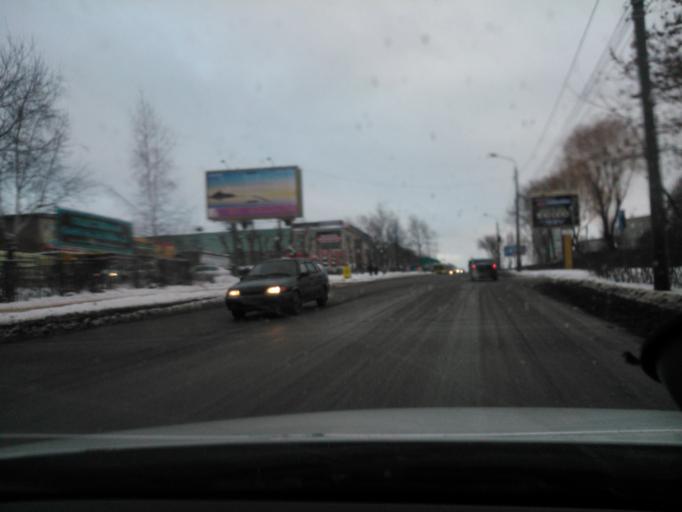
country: RU
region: Perm
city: Kondratovo
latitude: 57.9700
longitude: 56.1721
